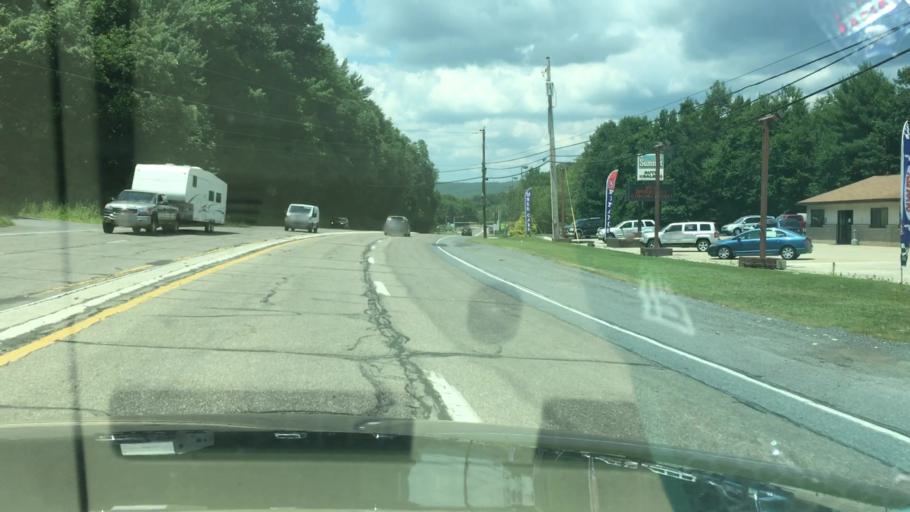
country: US
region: Pennsylvania
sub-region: Schuylkill County
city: Minersville
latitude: 40.6745
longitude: -76.2447
